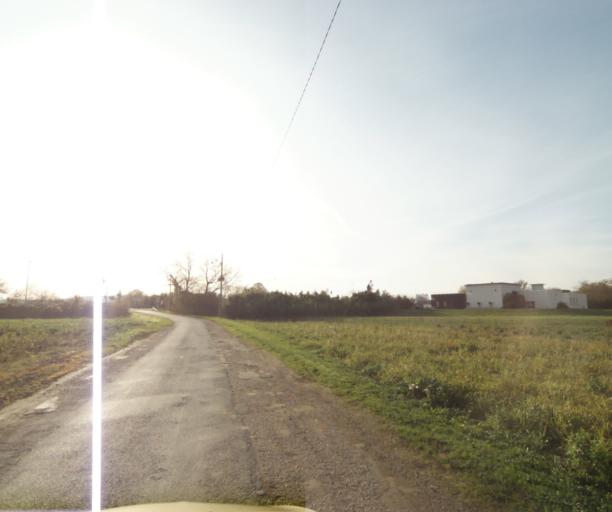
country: FR
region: Ile-de-France
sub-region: Departement des Yvelines
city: Chanteloup-les-Vignes
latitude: 48.9705
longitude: 2.0220
